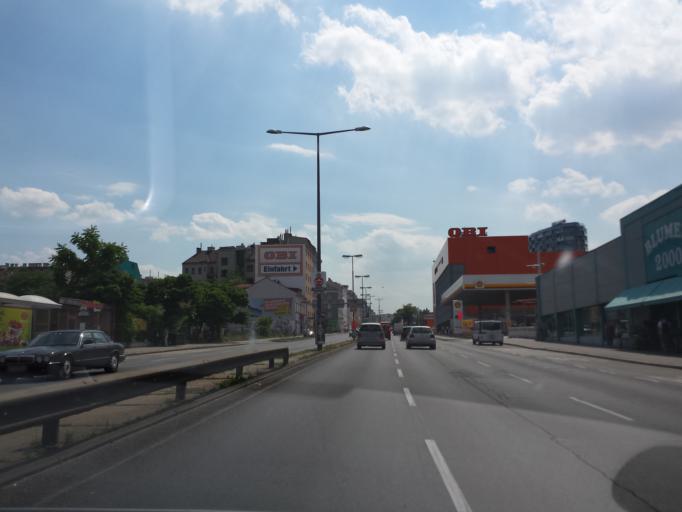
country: AT
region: Vienna
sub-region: Wien Stadt
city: Vienna
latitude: 48.1796
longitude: 16.3590
